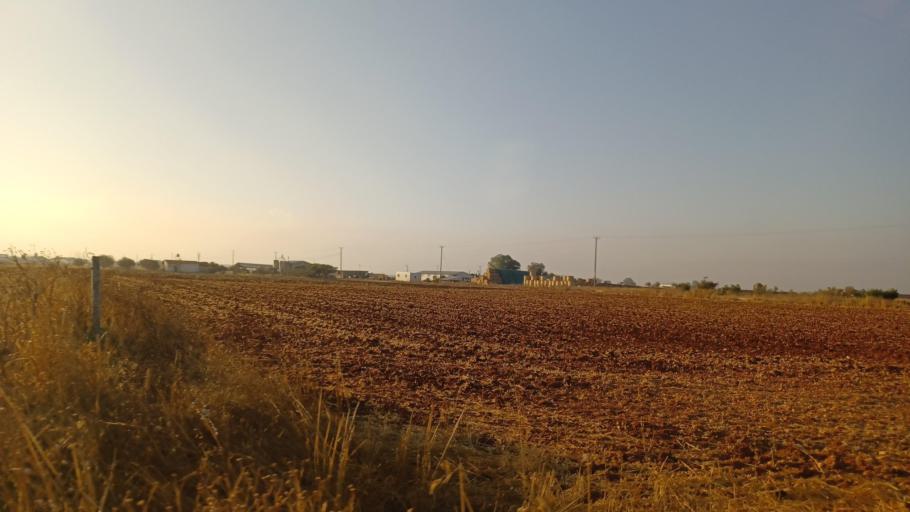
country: CY
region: Ammochostos
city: Avgorou
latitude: 35.0323
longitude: 33.8621
